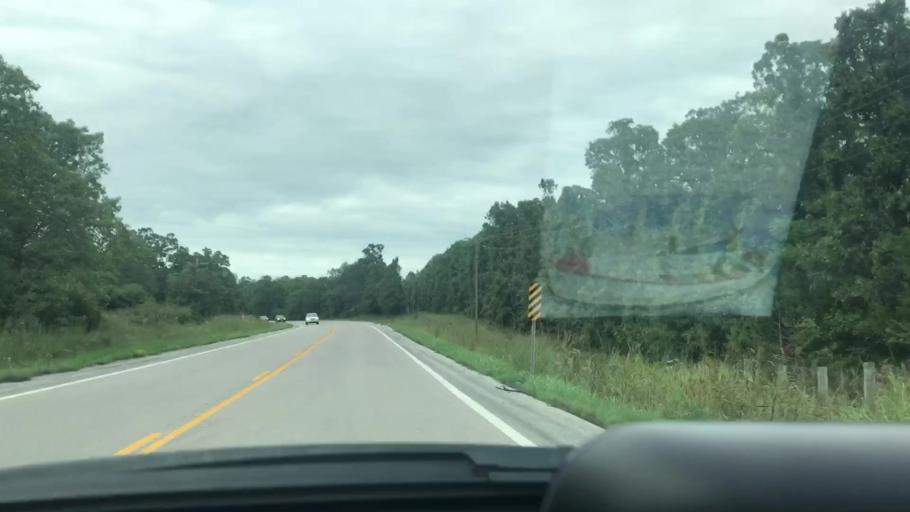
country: US
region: Missouri
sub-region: Benton County
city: Warsaw
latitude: 38.1578
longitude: -93.2972
